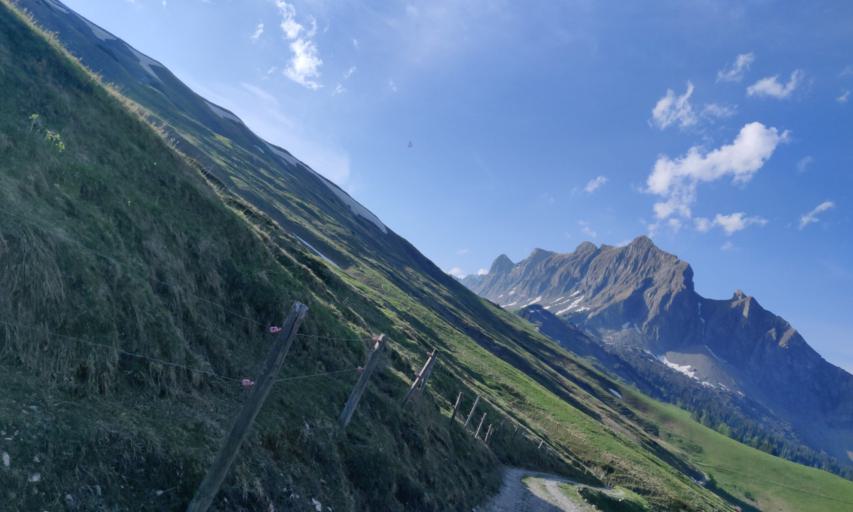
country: CH
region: Saint Gallen
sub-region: Wahlkreis Sarganserland
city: Sargans
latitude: 47.0745
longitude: 9.4300
